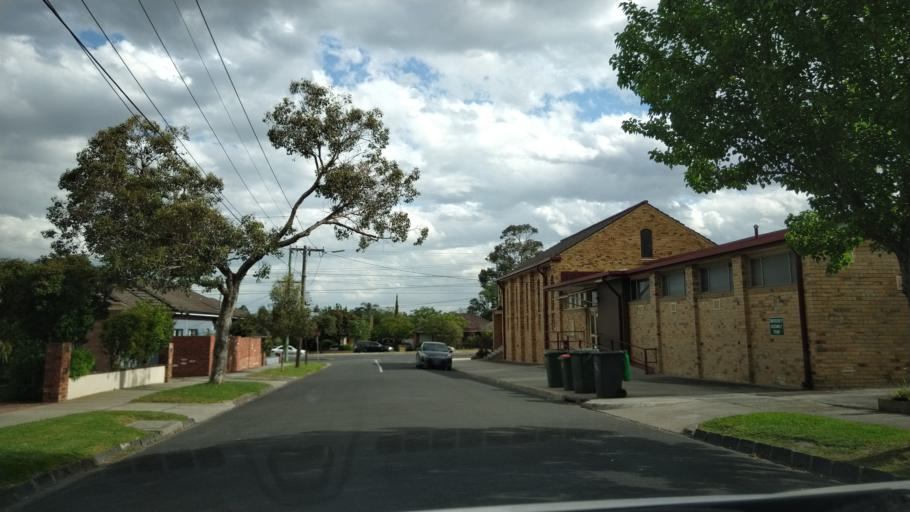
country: AU
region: Victoria
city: McKinnon
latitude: -37.9040
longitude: 145.0464
